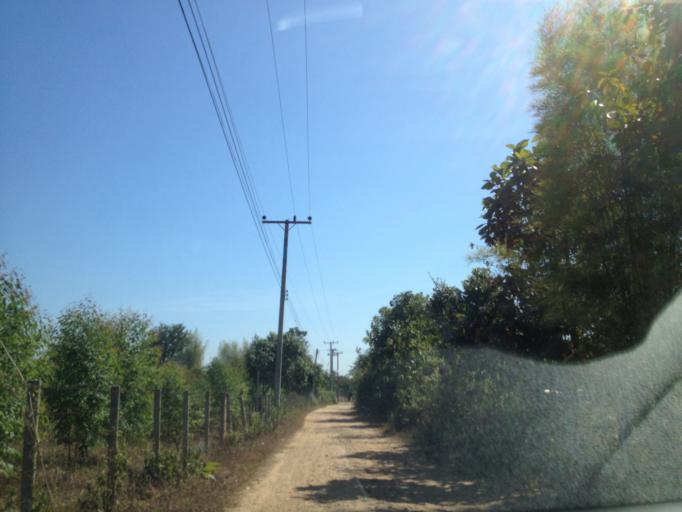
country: TH
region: Chiang Mai
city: San Pa Tong
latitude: 18.6690
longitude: 98.8717
